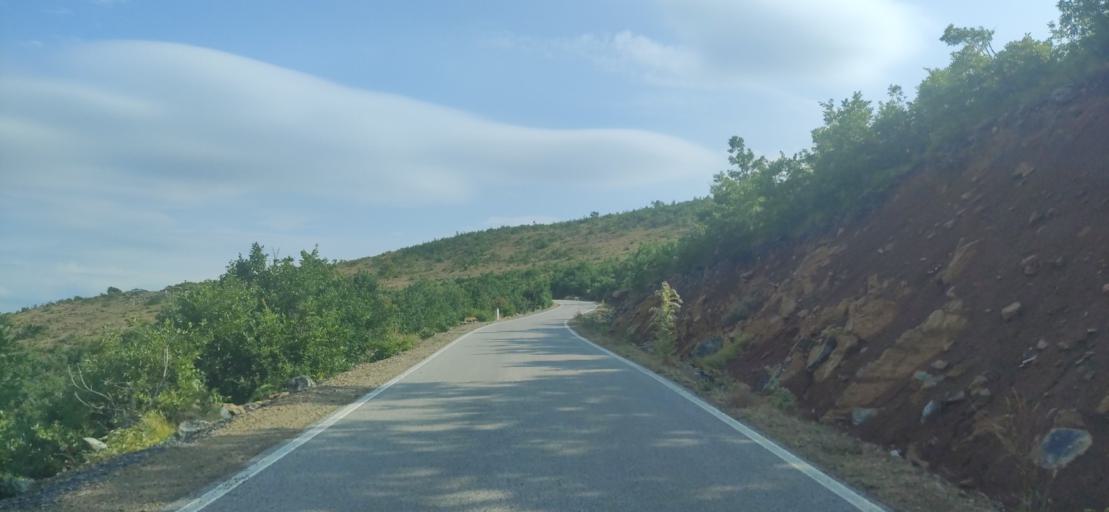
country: AL
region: Shkoder
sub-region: Rrethi i Pukes
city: Iballe
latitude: 42.1695
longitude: 20.0035
